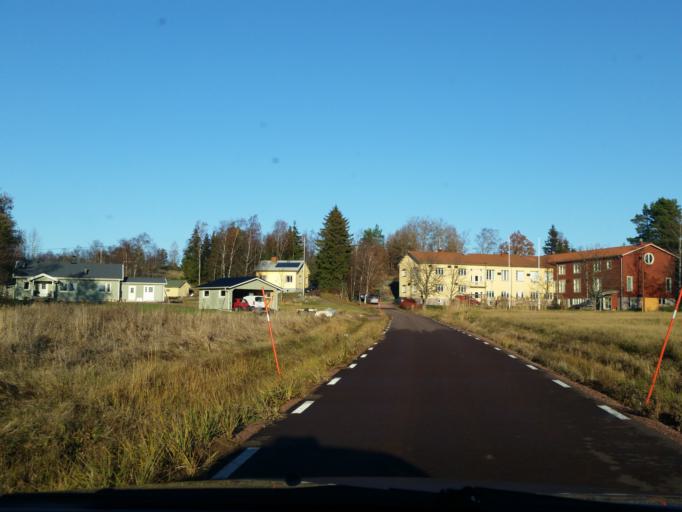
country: AX
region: Alands skaergard
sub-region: Braendoe
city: Braendoe
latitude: 60.4137
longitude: 21.0411
